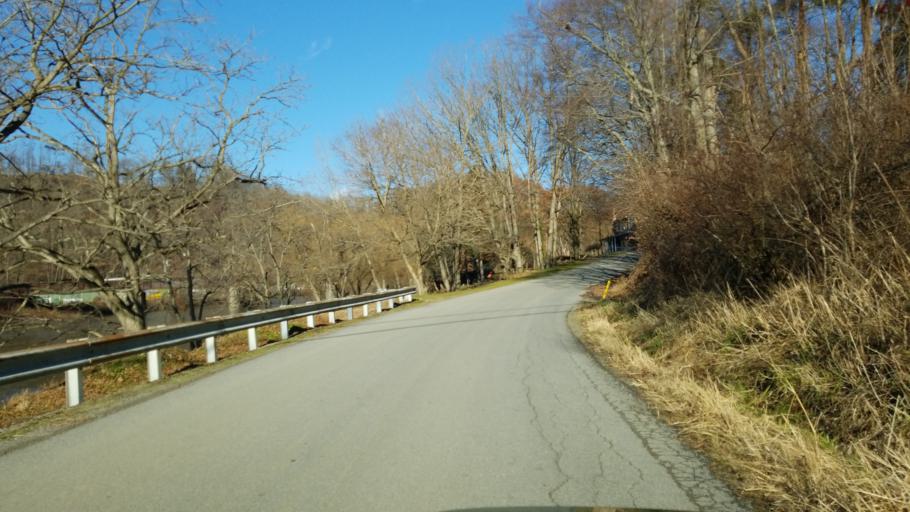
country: US
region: Pennsylvania
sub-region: Clearfield County
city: Curwensville
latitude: 40.9796
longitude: -78.4939
